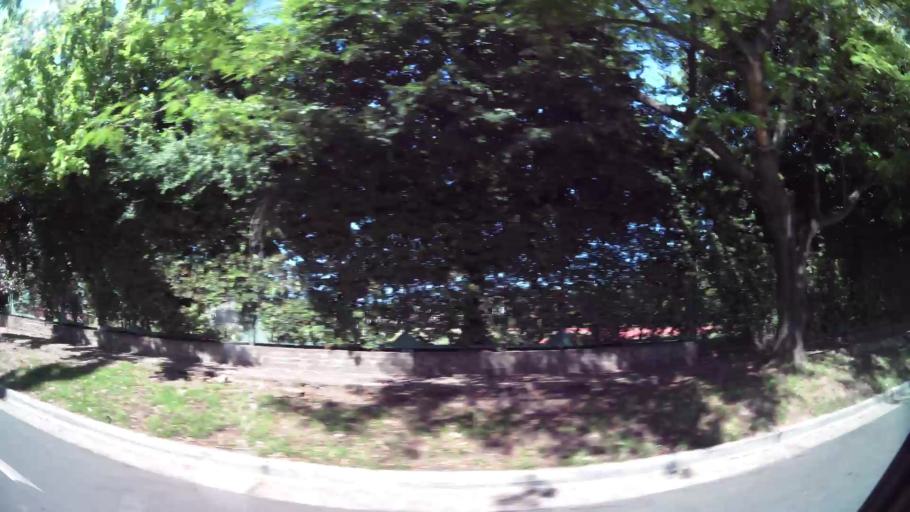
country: AR
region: Buenos Aires
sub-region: Partido de Tigre
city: Tigre
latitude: -34.4807
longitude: -58.5751
